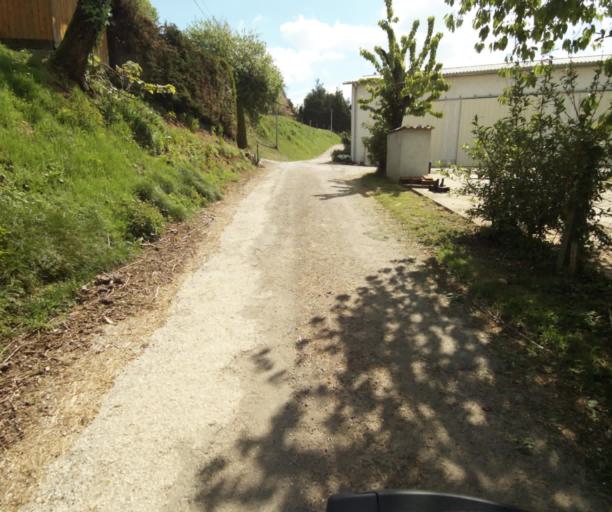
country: FR
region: Limousin
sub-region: Departement de la Correze
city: Naves
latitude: 45.2928
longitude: 1.7662
